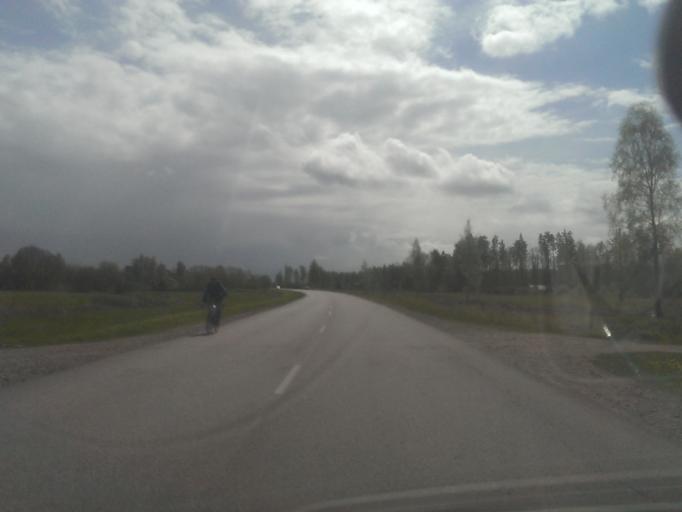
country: LV
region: Ventspils
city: Ventspils
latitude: 57.2883
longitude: 21.5664
